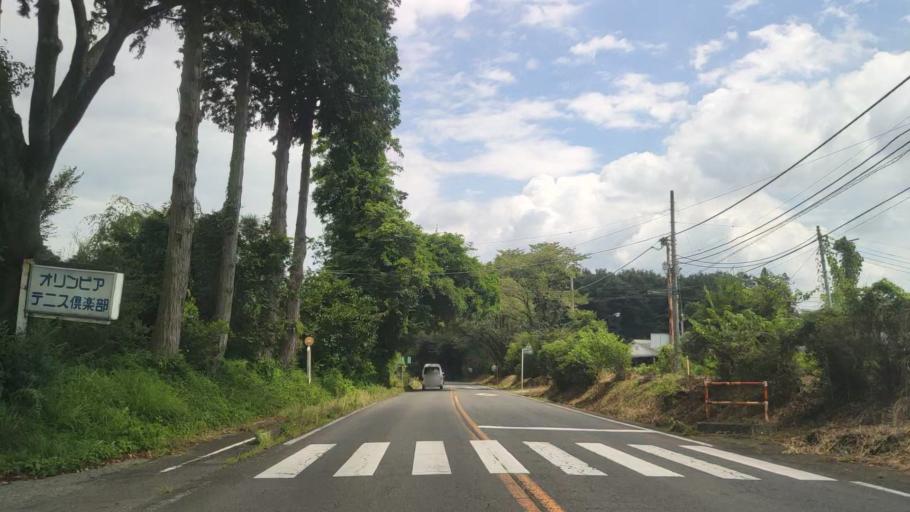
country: JP
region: Tochigi
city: Imaichi
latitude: 36.6779
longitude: 139.7985
